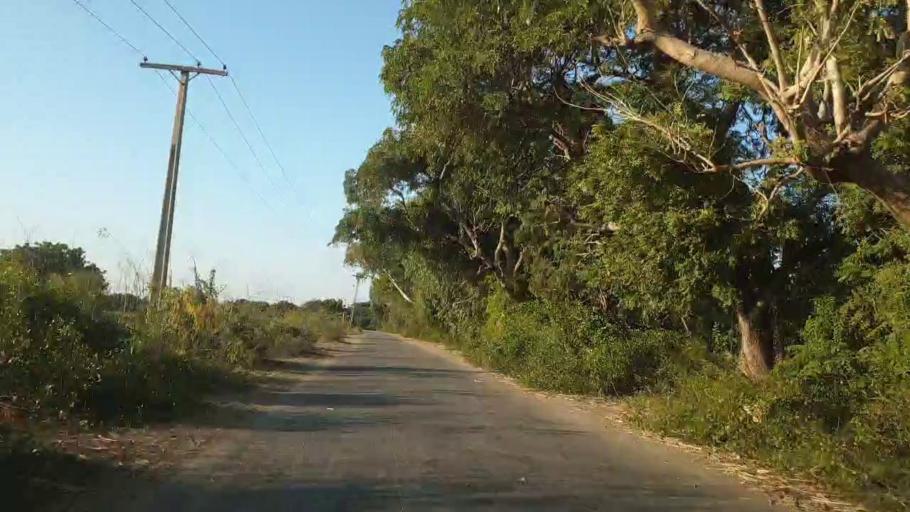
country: PK
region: Sindh
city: Mirpur Khas
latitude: 25.6551
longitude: 69.0970
